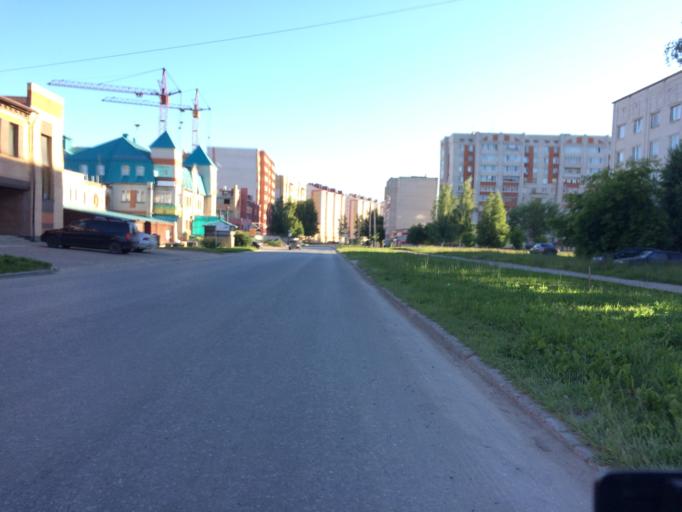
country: RU
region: Mariy-El
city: Medvedevo
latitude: 56.6434
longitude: 47.8352
